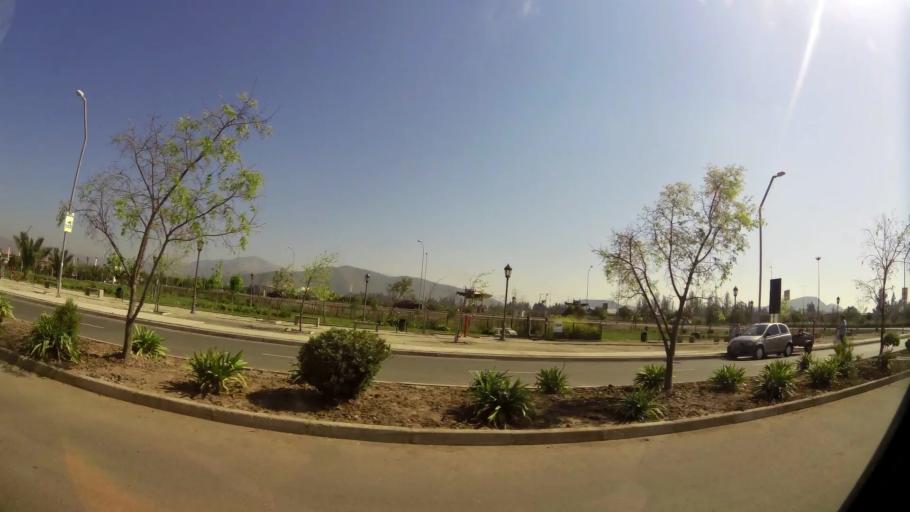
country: CL
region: Santiago Metropolitan
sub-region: Provincia de Talagante
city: Penaflor
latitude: -33.5607
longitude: -70.8283
